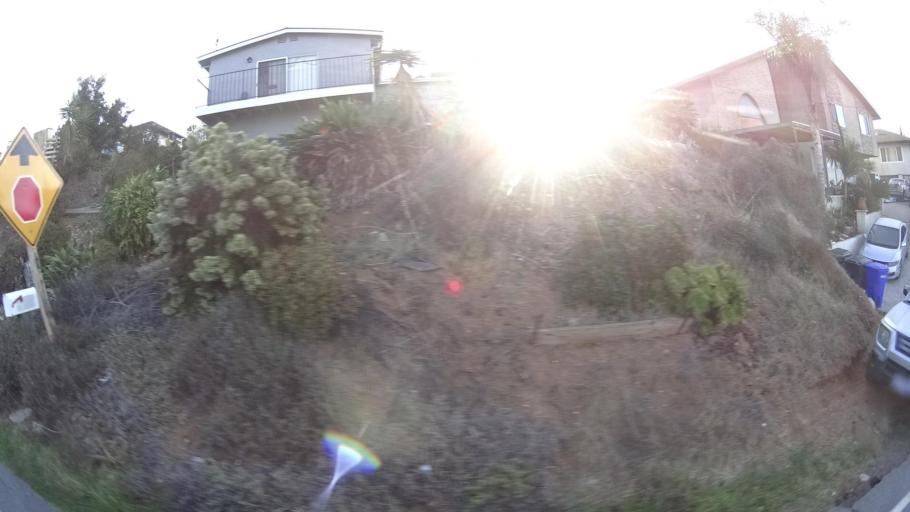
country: US
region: California
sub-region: San Diego County
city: La Presa
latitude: 32.7230
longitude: -117.0085
